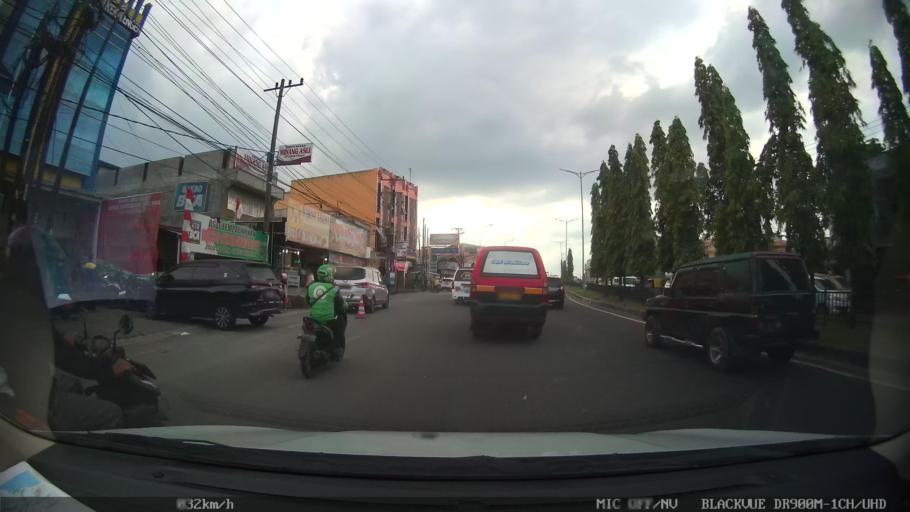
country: ID
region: North Sumatra
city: Deli Tua
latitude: 3.5406
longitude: 98.6586
